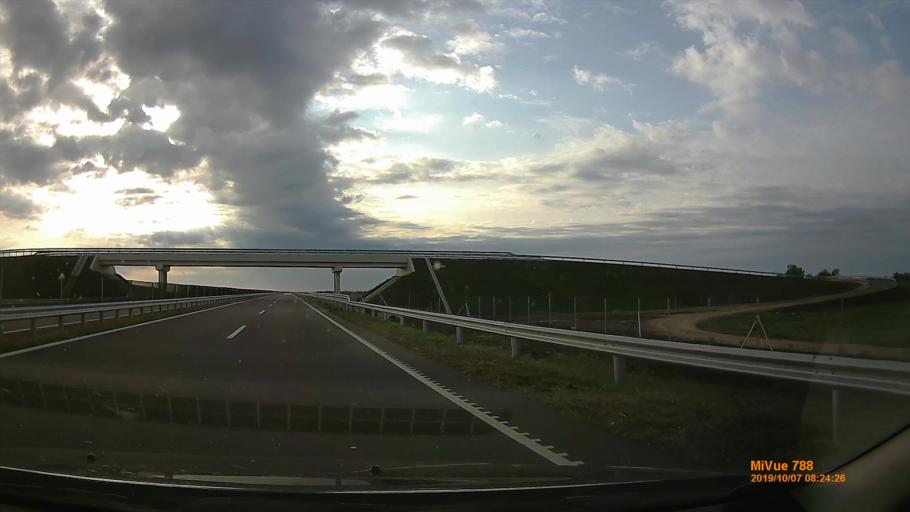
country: HU
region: Jasz-Nagykun-Szolnok
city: Kunszentmarton
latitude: 46.8385
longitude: 20.3413
